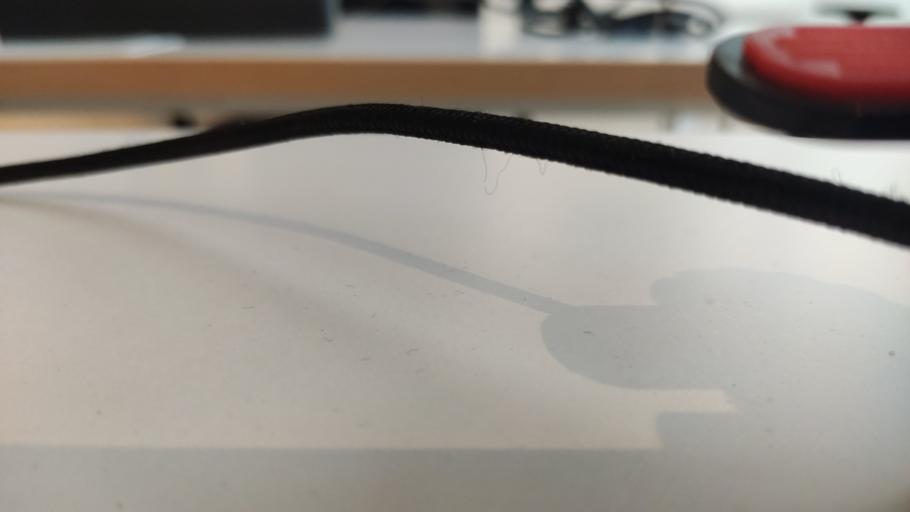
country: RU
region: Moskovskaya
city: Shevlyakovo
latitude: 56.3939
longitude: 36.8627
